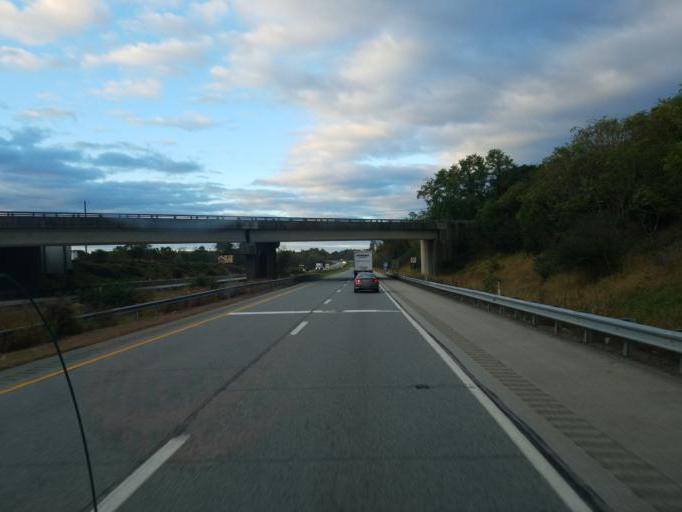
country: US
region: Pennsylvania
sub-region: York County
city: Shiloh
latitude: 39.9484
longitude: -76.7954
